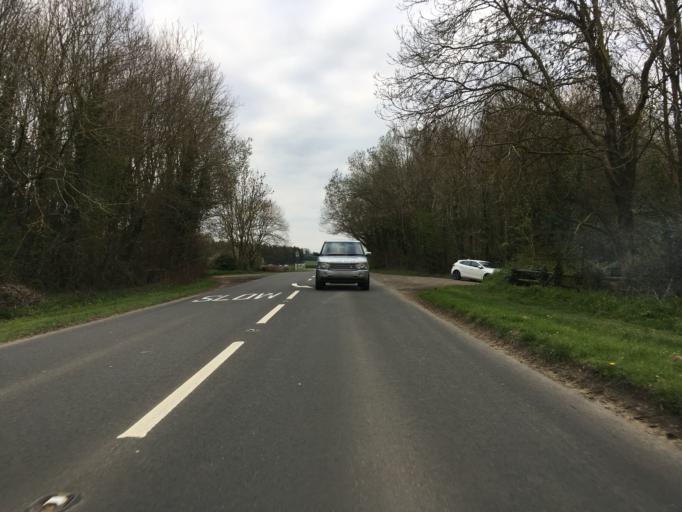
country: GB
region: England
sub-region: Gloucestershire
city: Coates
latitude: 51.6795
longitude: -2.0151
